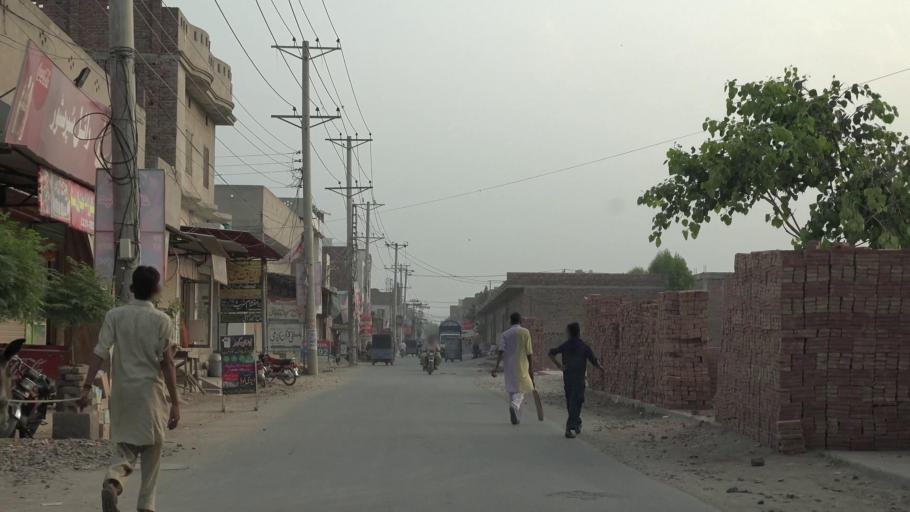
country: PK
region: Punjab
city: Faisalabad
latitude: 31.4297
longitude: 73.1401
